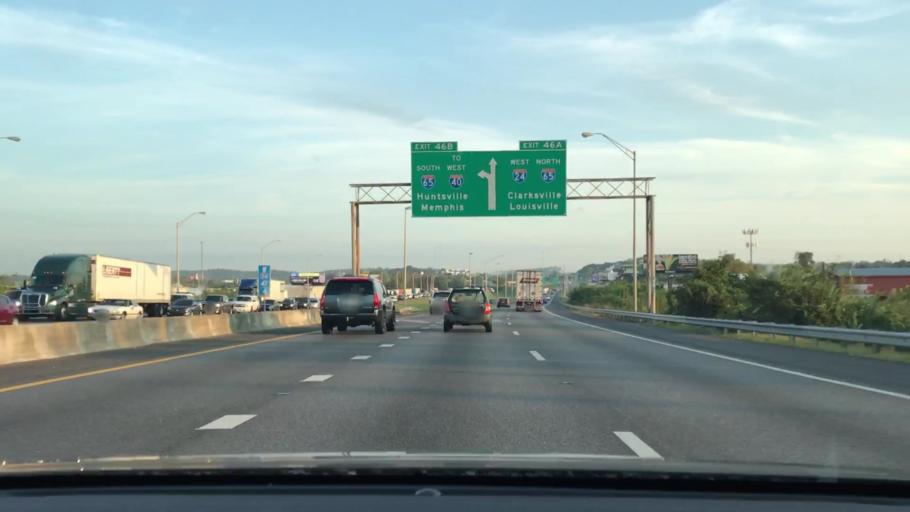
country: US
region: Tennessee
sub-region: Davidson County
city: Nashville
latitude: 36.1828
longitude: -86.7750
